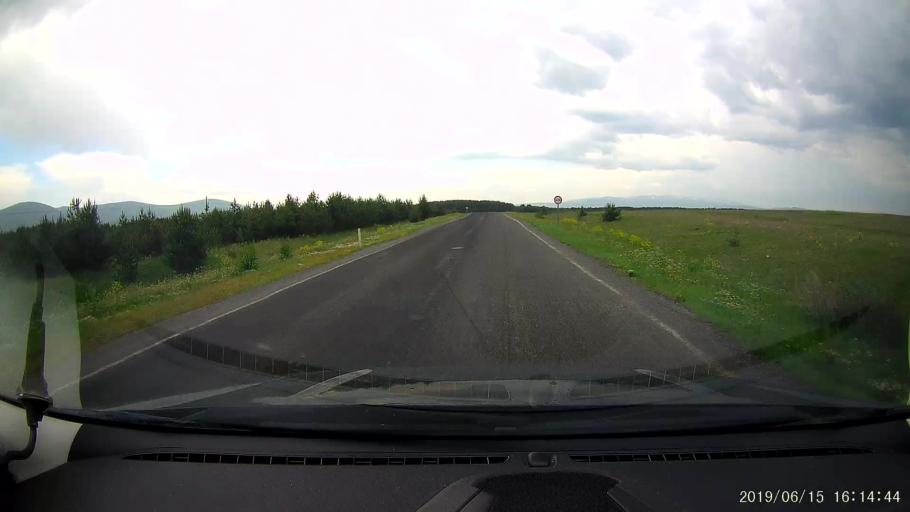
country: TR
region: Ardahan
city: Hanak
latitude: 41.2761
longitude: 42.8473
